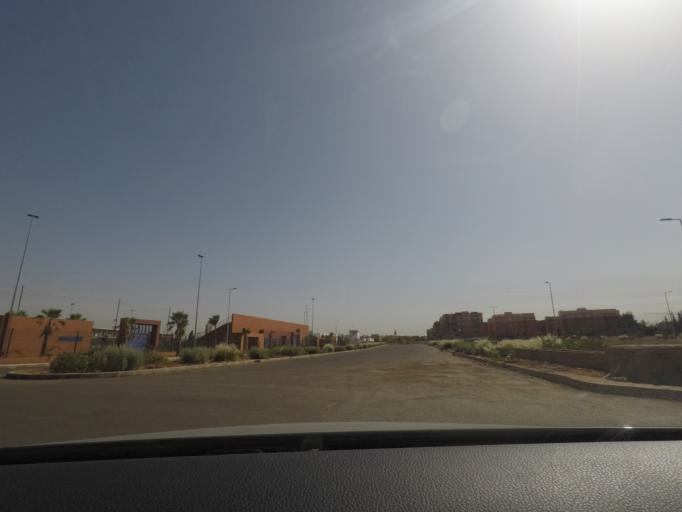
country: MA
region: Marrakech-Tensift-Al Haouz
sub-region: Marrakech
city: Marrakesh
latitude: 31.5877
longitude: -8.0307
